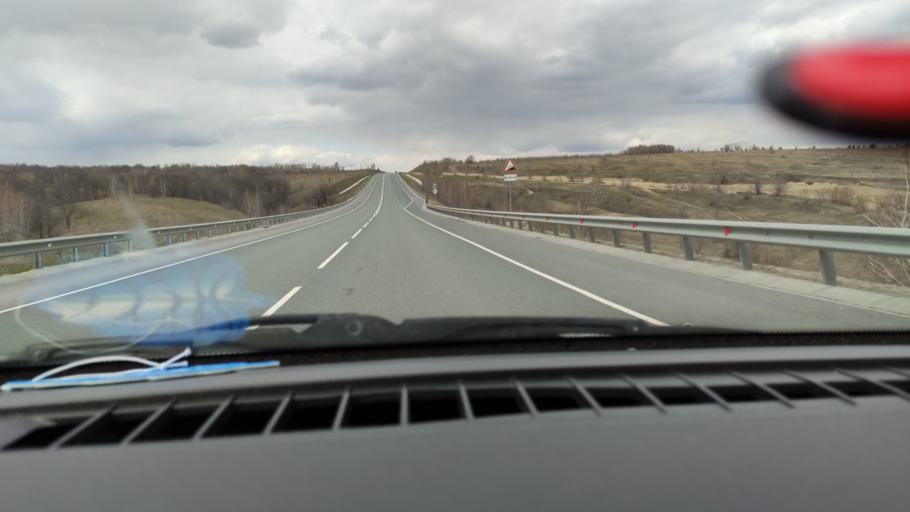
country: RU
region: Saratov
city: Shikhany
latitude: 52.1422
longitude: 47.2049
